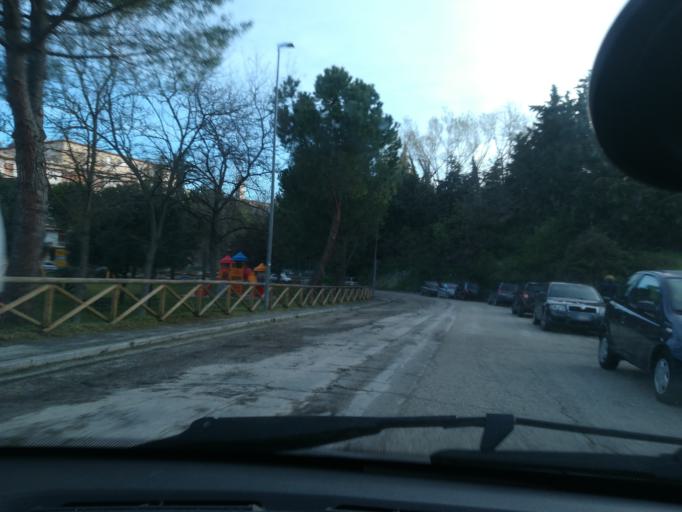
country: IT
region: The Marches
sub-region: Provincia di Macerata
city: Macerata
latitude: 43.2936
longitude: 13.4519
